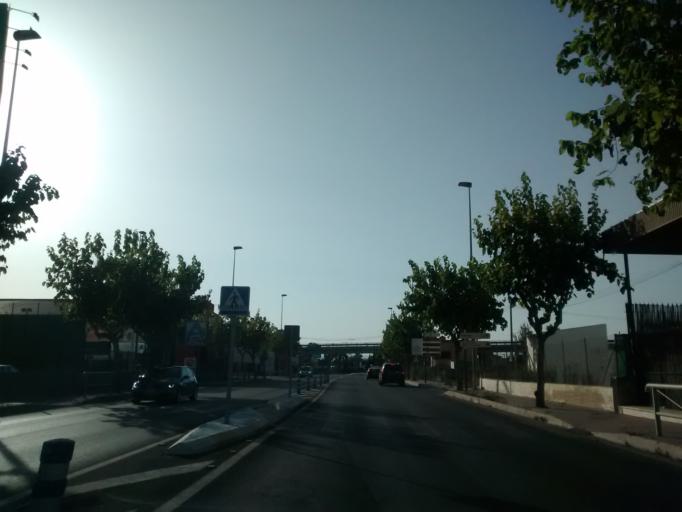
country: ES
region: Valencia
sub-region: Provincia de Alicante
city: Santa Pola
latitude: 38.1991
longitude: -0.5669
